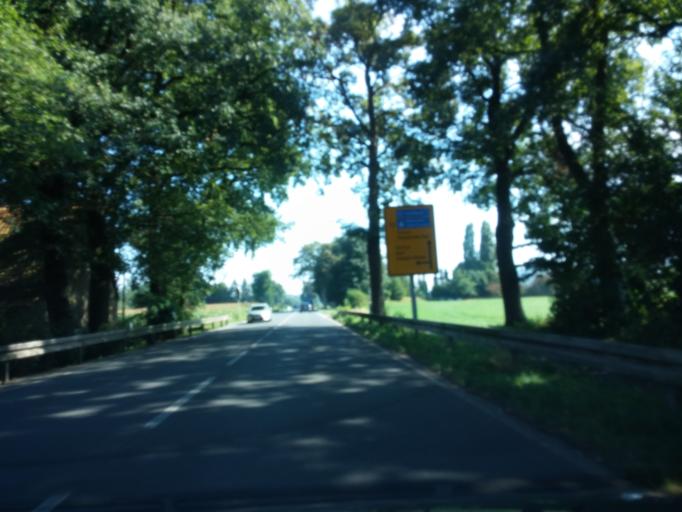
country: DE
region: North Rhine-Westphalia
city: Dorsten
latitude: 51.6348
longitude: 6.9986
